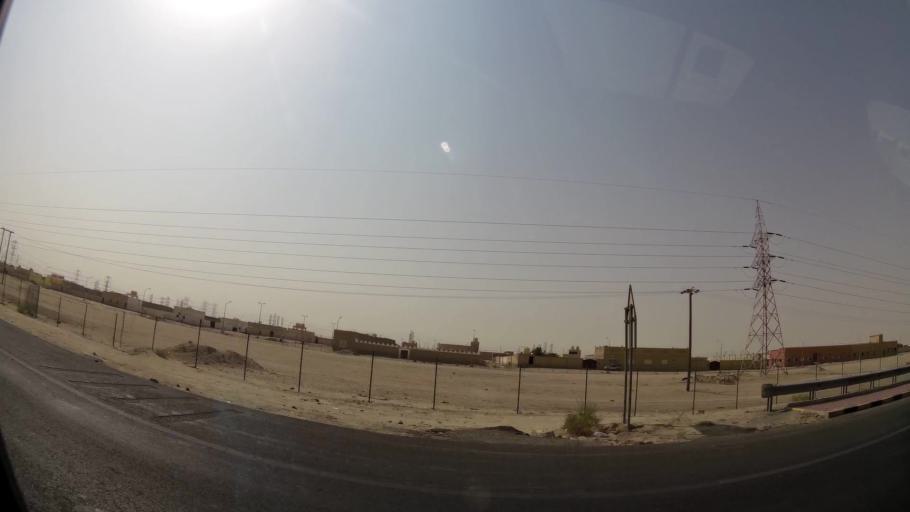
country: KW
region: Muhafazat al Jahra'
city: Al Jahra'
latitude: 29.3082
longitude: 47.6622
